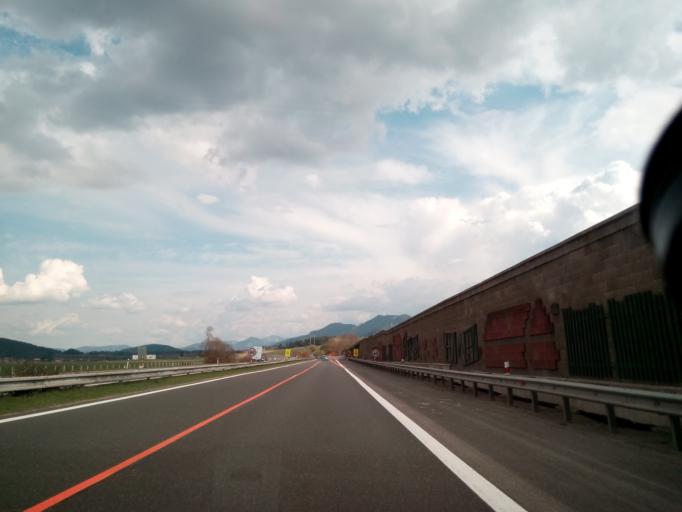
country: SK
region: Zilinsky
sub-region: Okres Liptovsky Mikulas
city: Liptovsky Mikulas
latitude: 49.0628
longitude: 19.6514
